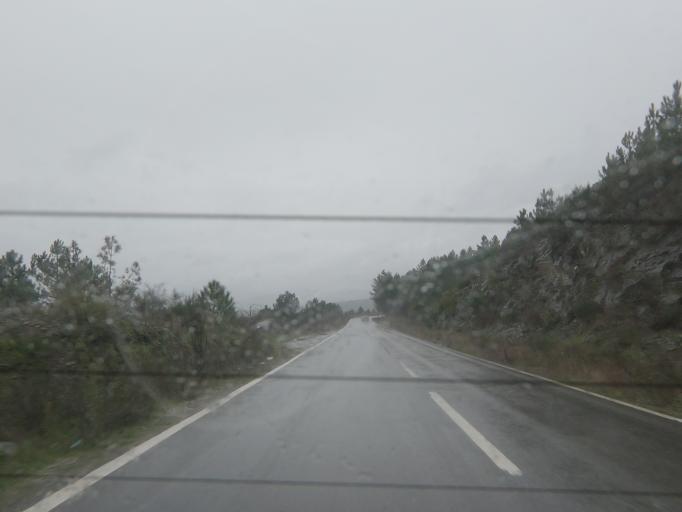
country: PT
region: Vila Real
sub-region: Sabrosa
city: Vilela
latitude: 41.2309
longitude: -7.6798
